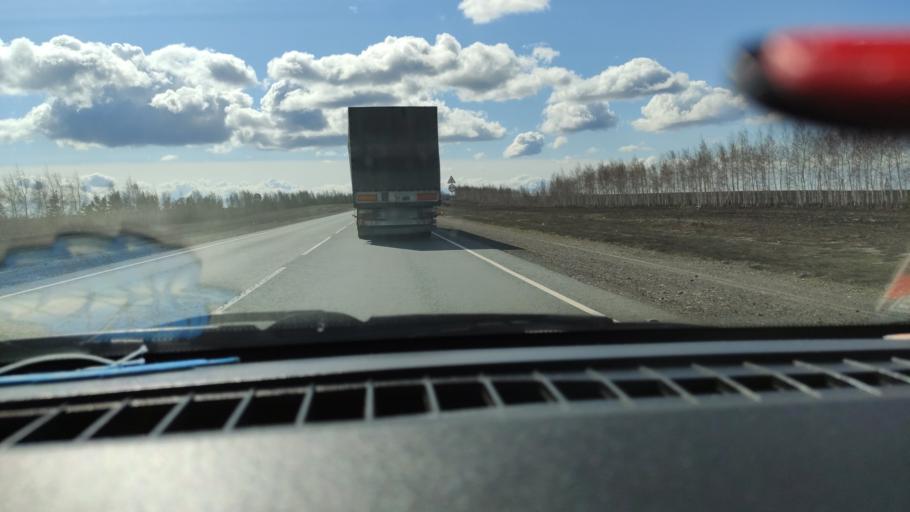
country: RU
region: Samara
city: Syzran'
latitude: 52.9364
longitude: 48.3075
